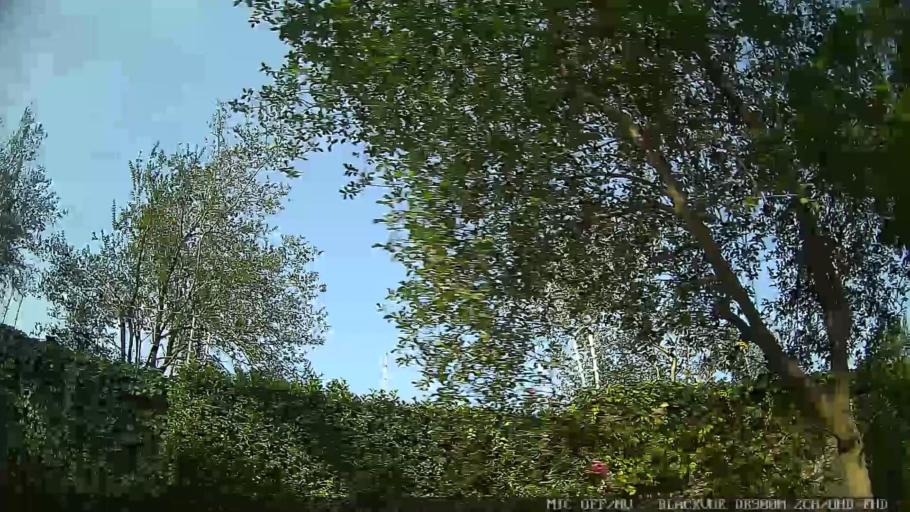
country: BR
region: Sao Paulo
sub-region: Taboao Da Serra
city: Taboao da Serra
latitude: -23.6130
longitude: -46.7162
